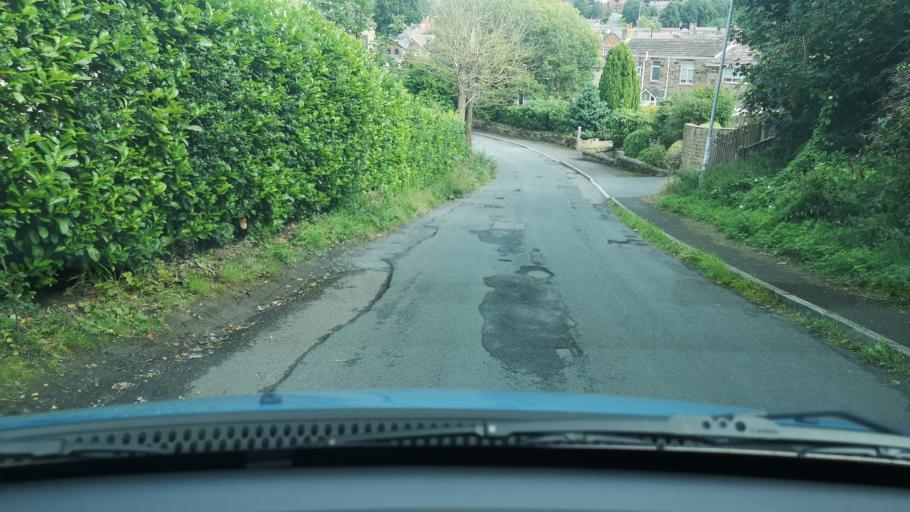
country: GB
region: England
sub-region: Kirklees
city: Heckmondwike
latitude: 53.7297
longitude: -1.6713
